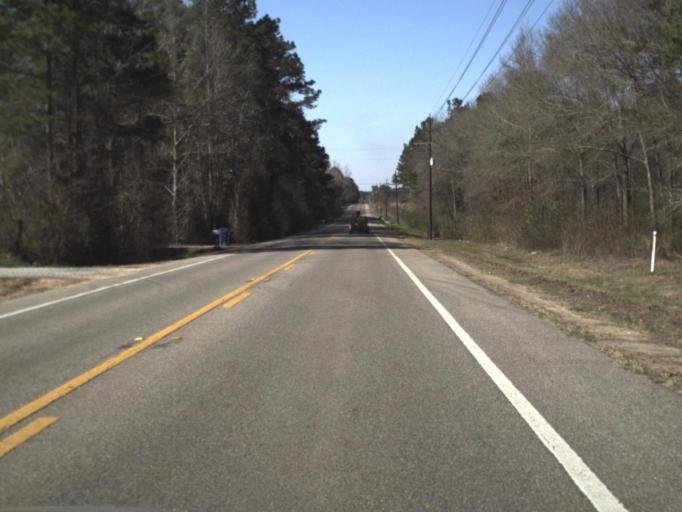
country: US
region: Florida
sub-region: Calhoun County
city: Blountstown
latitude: 30.5082
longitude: -85.1200
